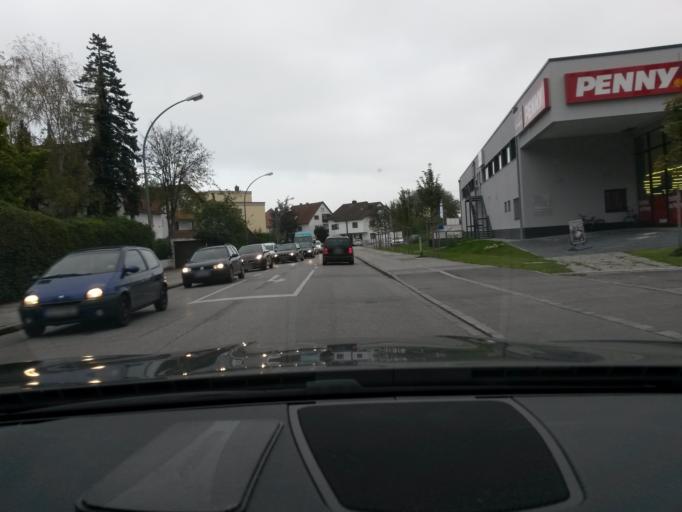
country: DE
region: Bavaria
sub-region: Lower Bavaria
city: Landshut
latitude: 48.5505
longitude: 12.1401
